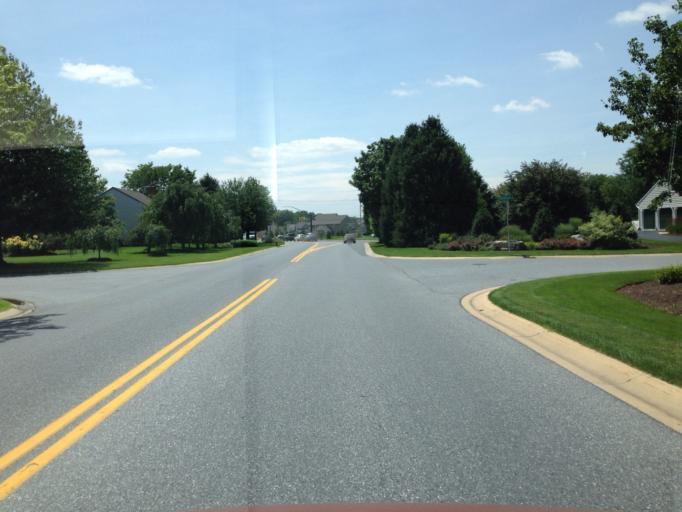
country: US
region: Pennsylvania
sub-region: Lancaster County
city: East Petersburg
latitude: 40.1097
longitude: -76.3325
